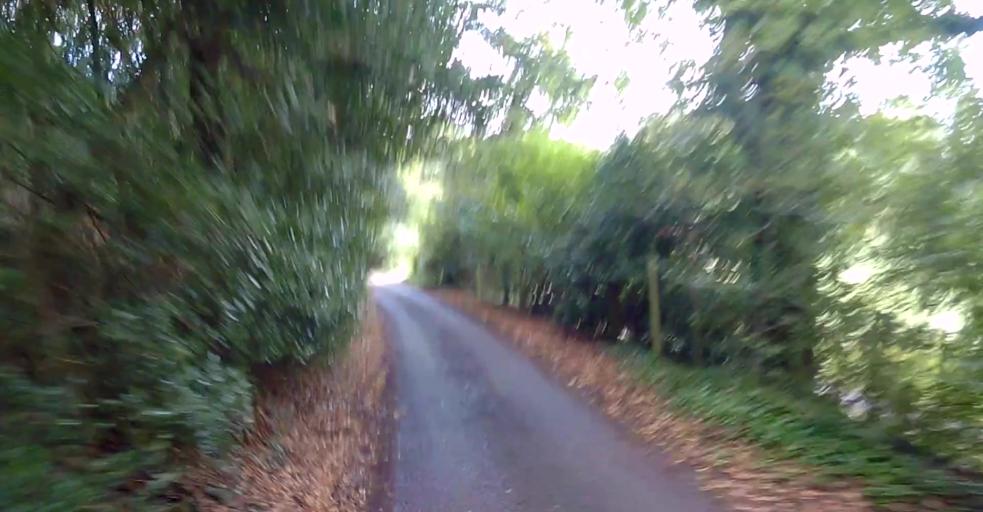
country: GB
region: England
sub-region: Surrey
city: Elstead
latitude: 51.1860
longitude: -0.7446
